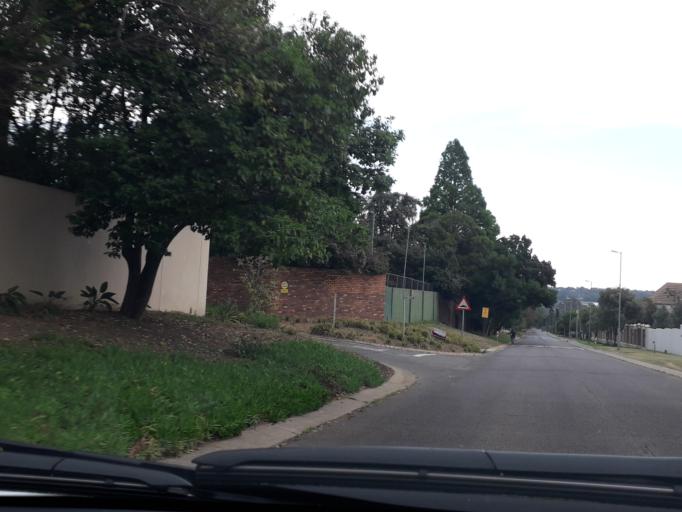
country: ZA
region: Gauteng
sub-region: City of Johannesburg Metropolitan Municipality
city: Johannesburg
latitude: -26.0875
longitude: 28.0363
